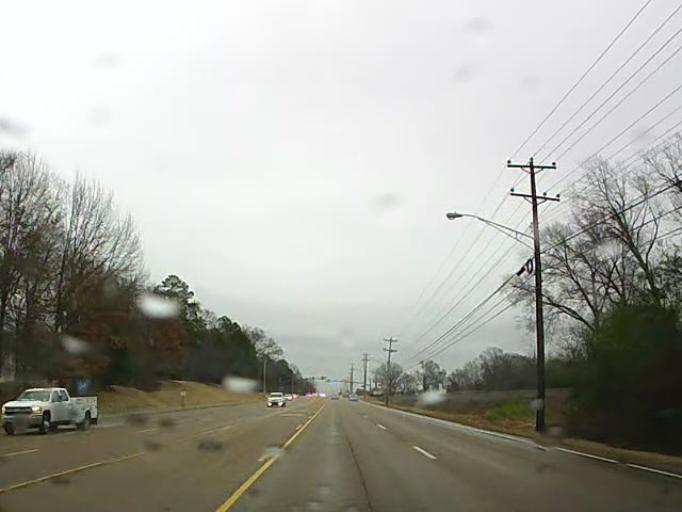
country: US
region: Tennessee
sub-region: Shelby County
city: Collierville
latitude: 35.0475
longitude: -89.7143
